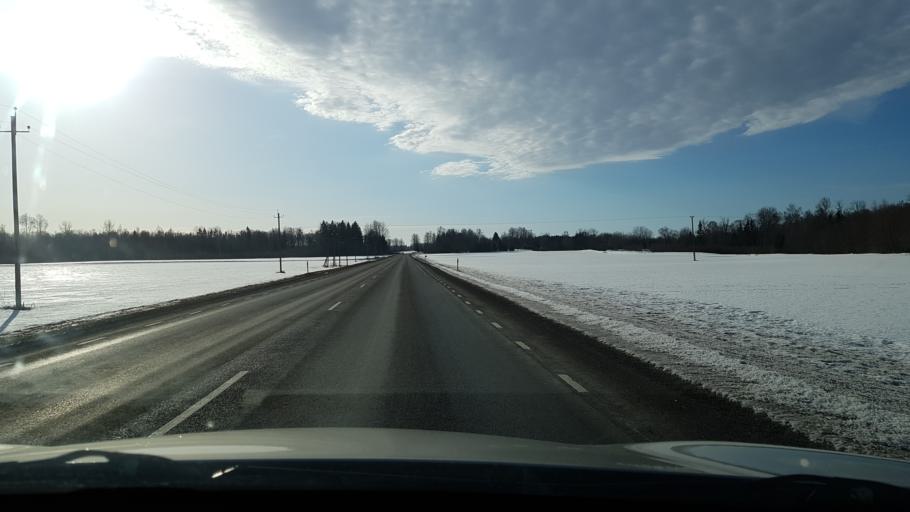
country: EE
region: Viljandimaa
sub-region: Viljandi linn
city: Viljandi
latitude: 58.4543
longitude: 25.5944
